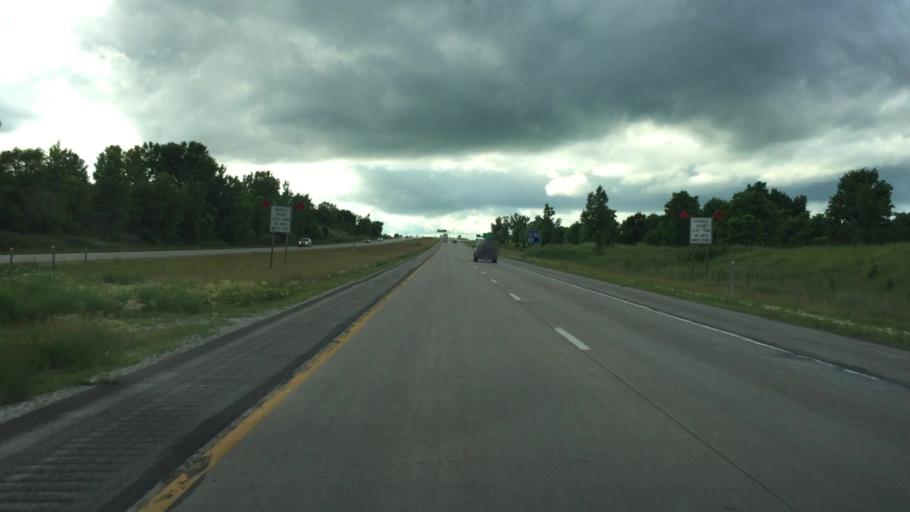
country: US
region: Iowa
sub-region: Polk County
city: Altoona
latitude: 41.6350
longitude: -93.5043
